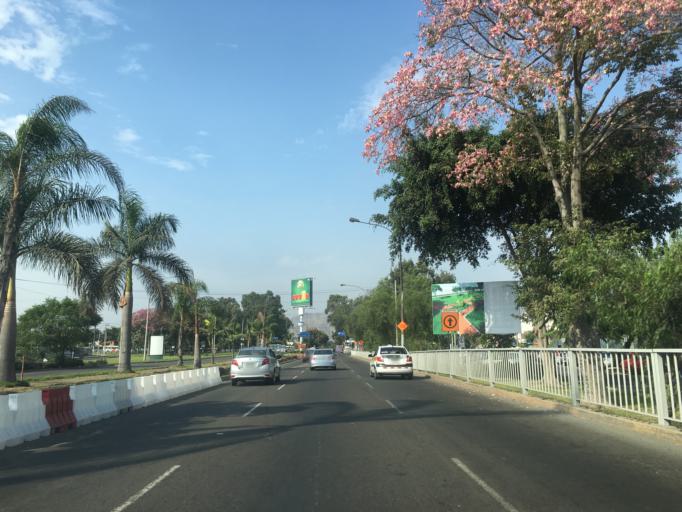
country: PE
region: Lima
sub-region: Lima
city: La Molina
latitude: -12.0726
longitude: -76.9588
